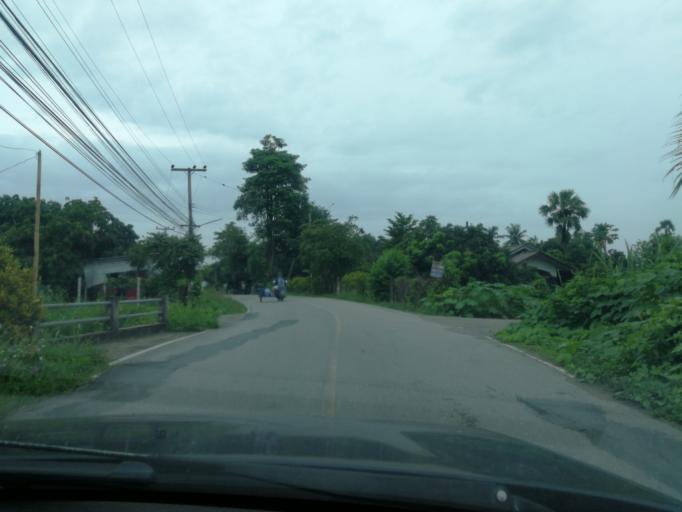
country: TH
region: Chiang Mai
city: San Pa Tong
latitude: 18.6038
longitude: 98.9071
